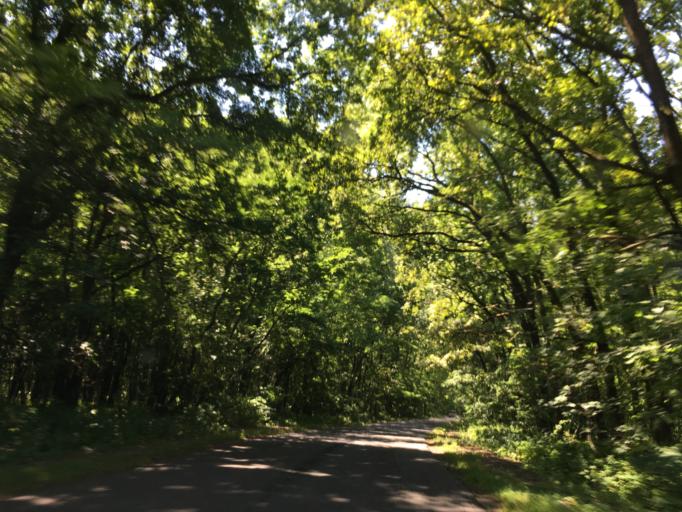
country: HU
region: Hajdu-Bihar
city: Mikepercs
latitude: 47.4702
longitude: 21.7006
